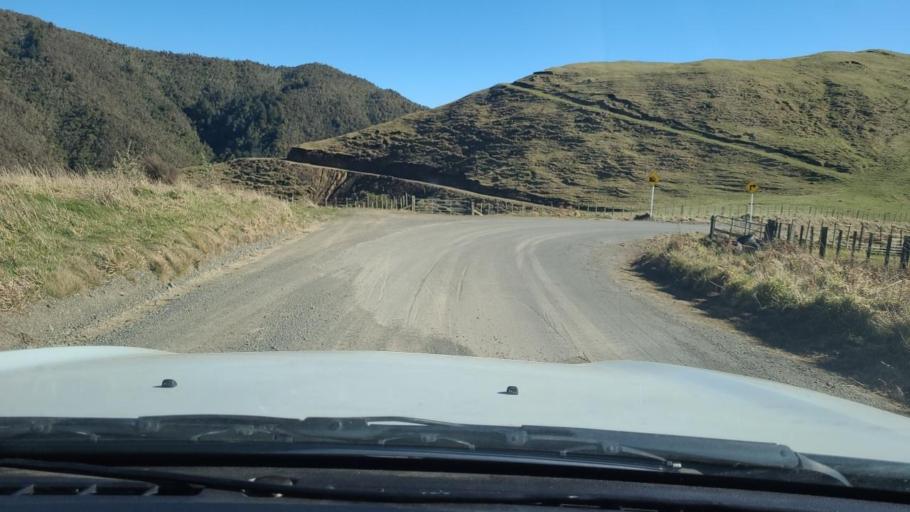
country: NZ
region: Hawke's Bay
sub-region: Napier City
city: Taradale
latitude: -39.2383
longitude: 176.4954
